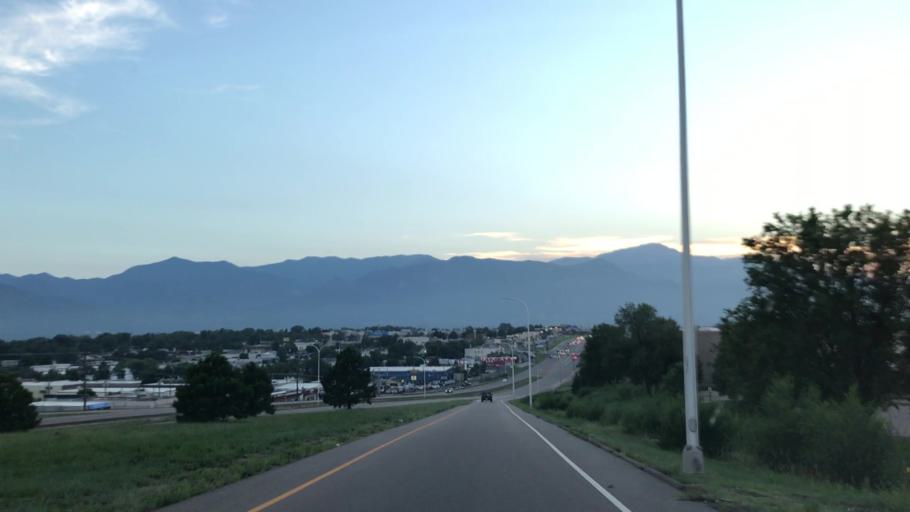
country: US
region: Colorado
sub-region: El Paso County
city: Cimarron Hills
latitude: 38.8403
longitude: -104.7583
